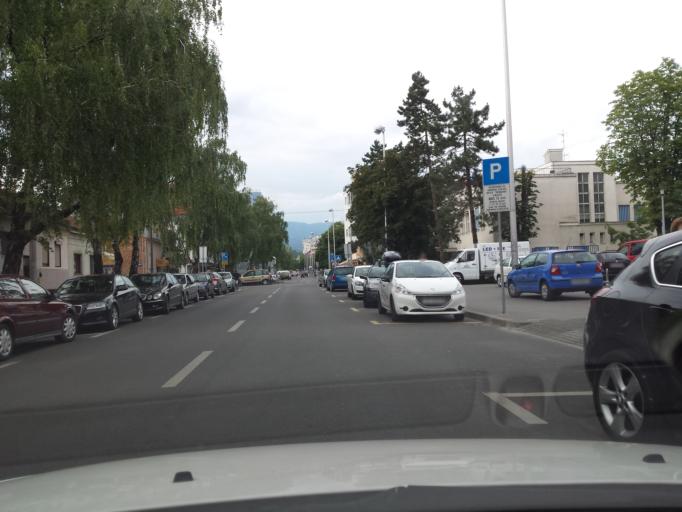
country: HR
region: Grad Zagreb
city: Zagreb - Centar
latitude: 45.8007
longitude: 15.9537
